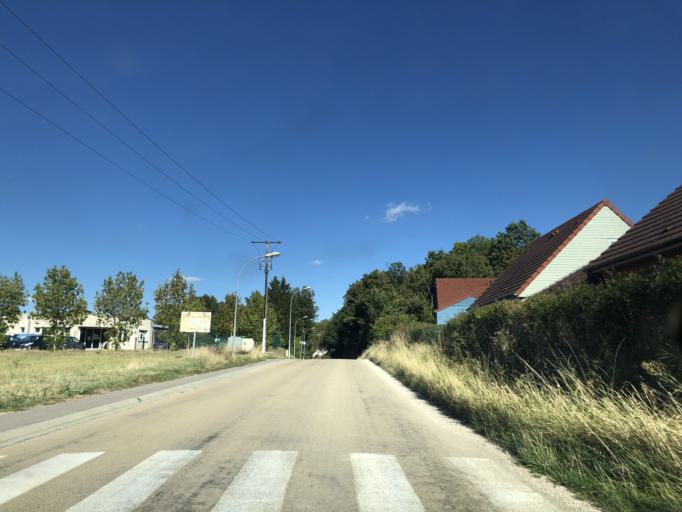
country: FR
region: Bourgogne
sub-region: Departement de l'Yonne
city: Seignelay
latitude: 47.9011
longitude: 3.5933
